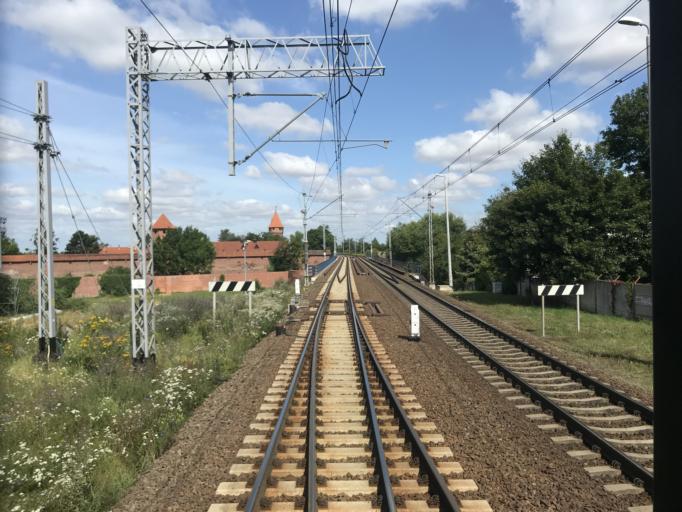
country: PL
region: Pomeranian Voivodeship
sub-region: Powiat malborski
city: Malbork
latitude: 54.0408
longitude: 19.0347
